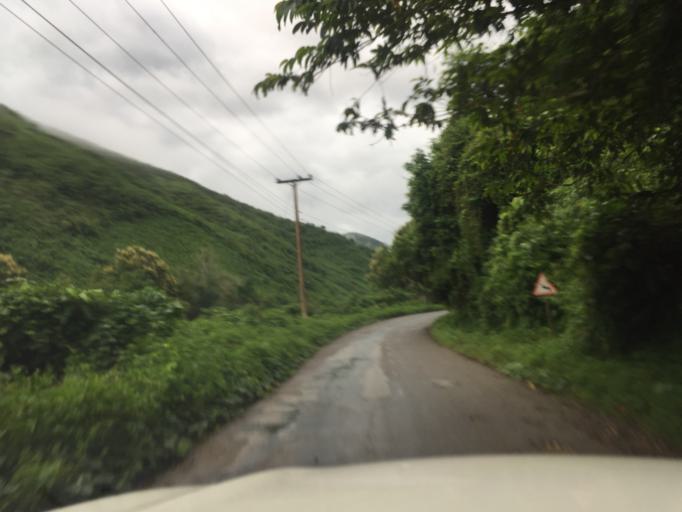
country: LA
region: Oudomxai
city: Muang La
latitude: 21.0410
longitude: 102.2413
